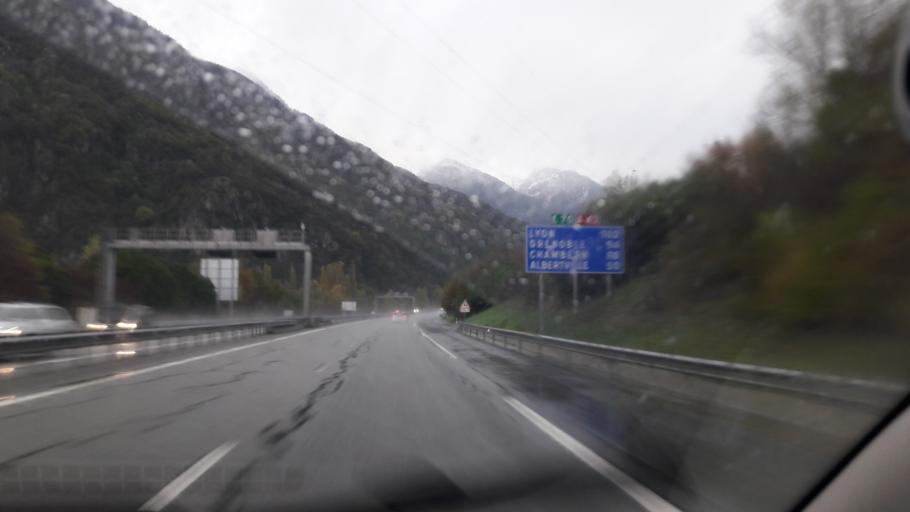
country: FR
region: Rhone-Alpes
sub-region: Departement de la Savoie
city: Saint-Etienne-de-Cuines
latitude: 45.3519
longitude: 6.2935
